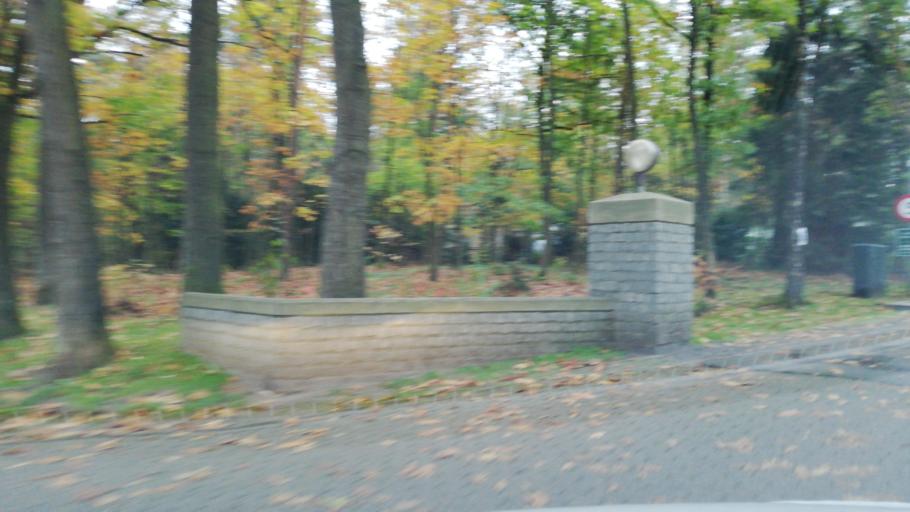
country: NL
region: Gelderland
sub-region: Gemeente Apeldoorn
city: Beekbergen
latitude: 52.1331
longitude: 5.9635
